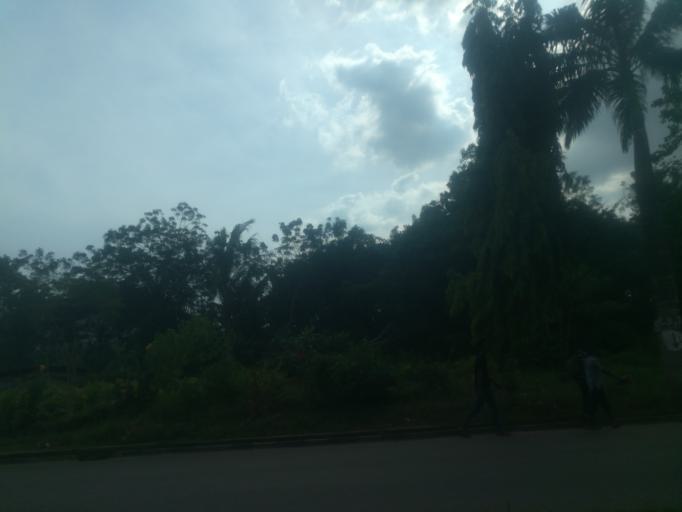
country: NG
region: Ogun
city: Abeokuta
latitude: 7.1367
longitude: 3.3446
